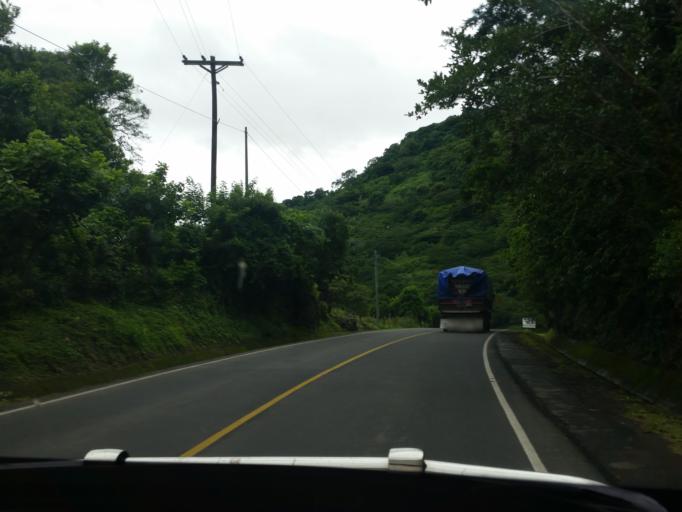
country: NI
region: Jinotega
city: Jinotega
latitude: 13.1177
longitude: -86.0058
